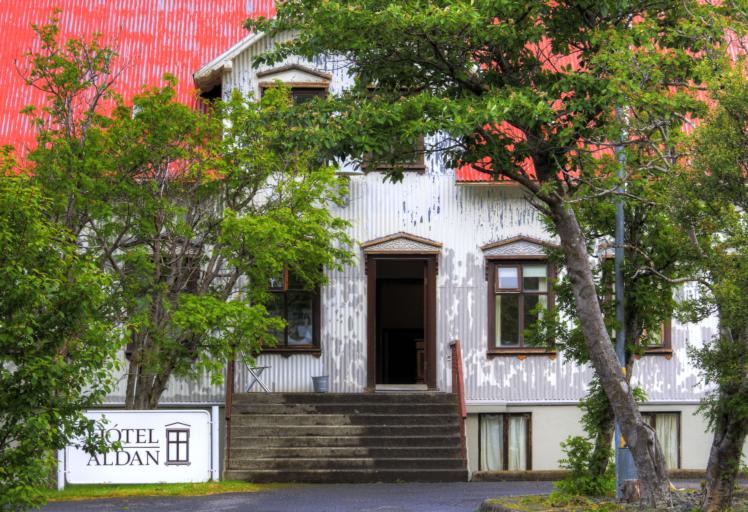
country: IS
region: East
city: Eskifjoerdur
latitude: 65.2615
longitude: -14.0094
